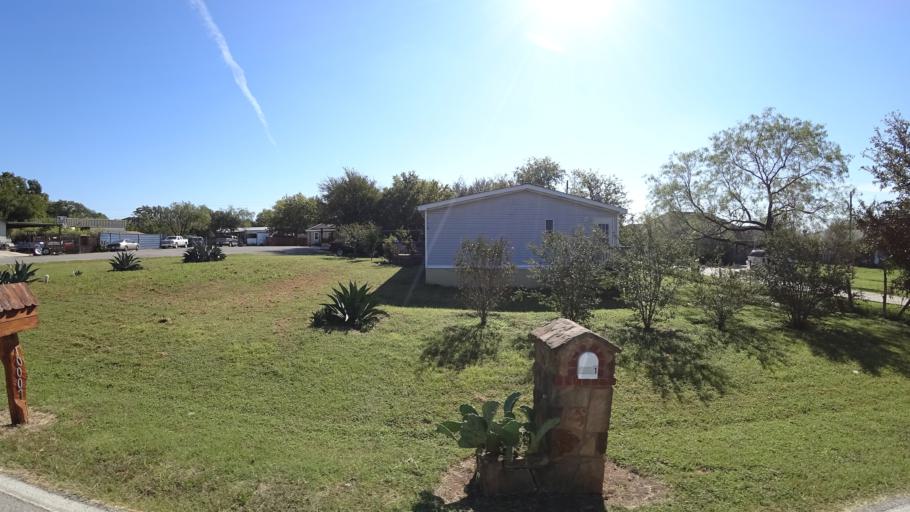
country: US
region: Texas
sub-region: Travis County
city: Hornsby Bend
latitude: 30.2686
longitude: -97.6240
